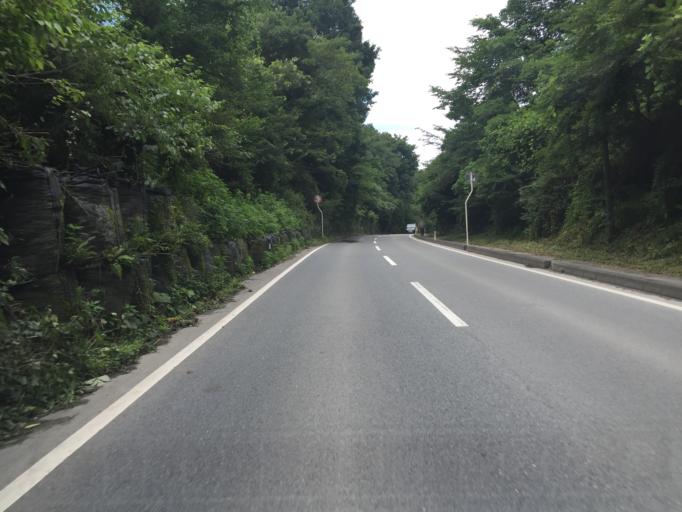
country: JP
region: Miyagi
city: Marumori
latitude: 37.7581
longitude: 140.9157
